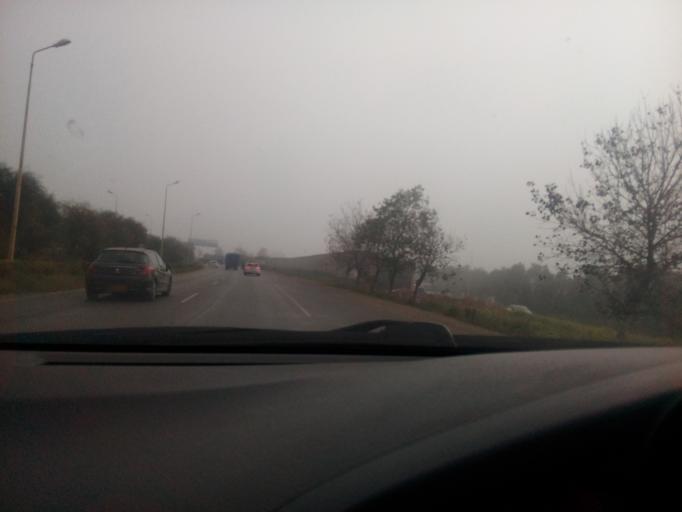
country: DZ
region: Oran
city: Es Senia
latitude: 35.6533
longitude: -0.6345
